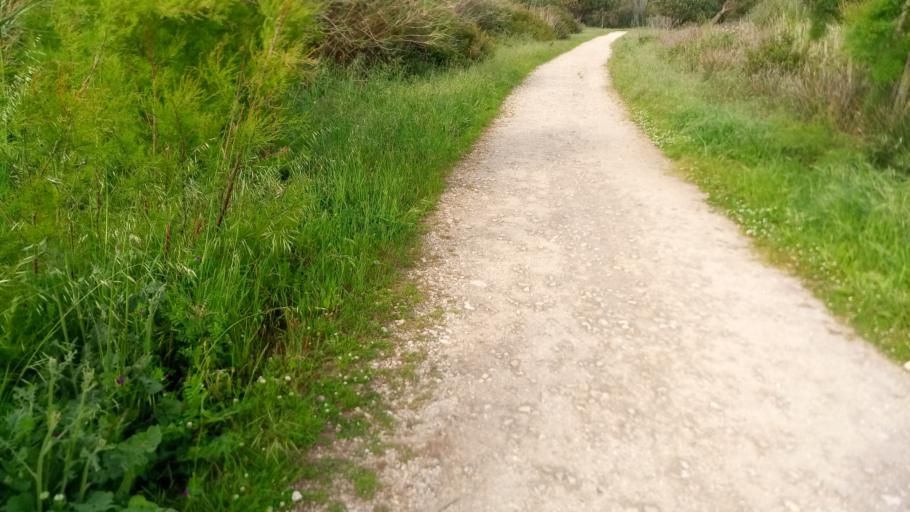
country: PT
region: Leiria
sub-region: Obidos
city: Obidos
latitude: 39.3984
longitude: -9.1995
